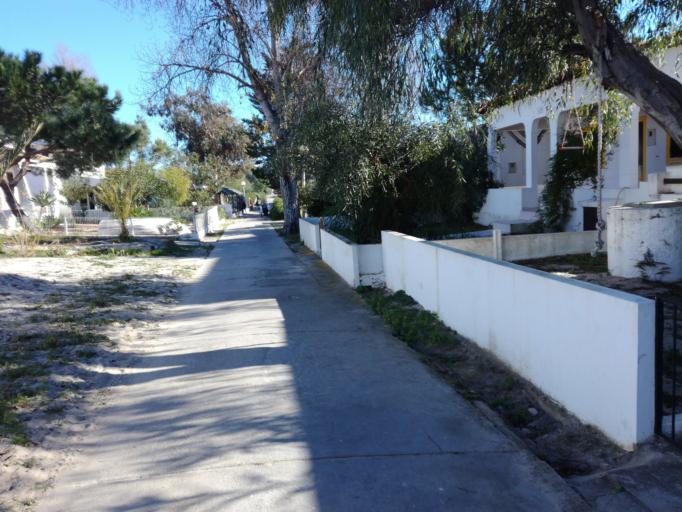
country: PT
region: Faro
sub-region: Olhao
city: Olhao
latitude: 37.0196
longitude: -7.8035
